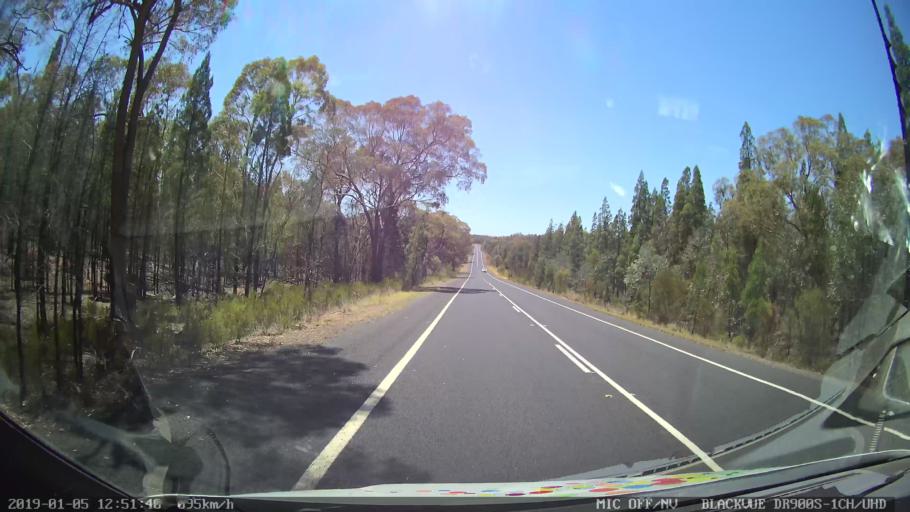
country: AU
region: New South Wales
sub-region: Warrumbungle Shire
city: Coonabarabran
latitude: -31.1212
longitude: 149.6433
